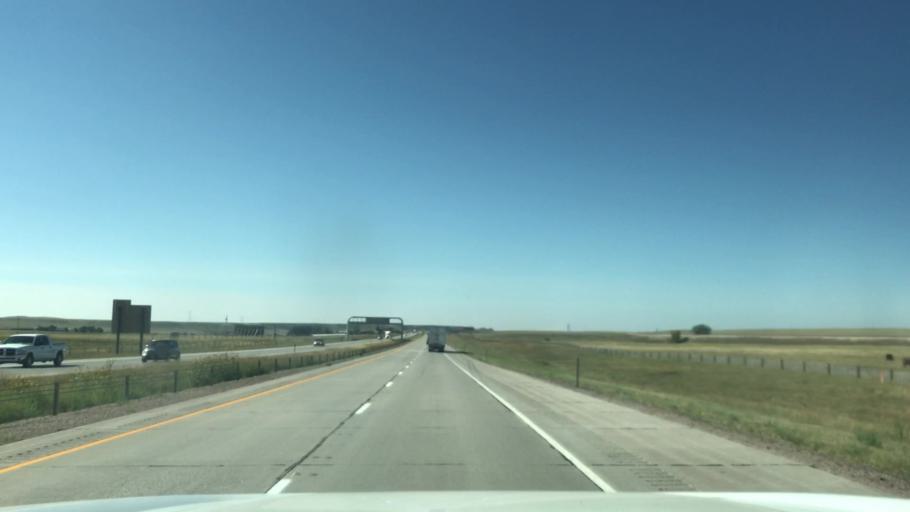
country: US
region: Wyoming
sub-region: Laramie County
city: South Greeley
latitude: 41.0193
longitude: -104.9037
